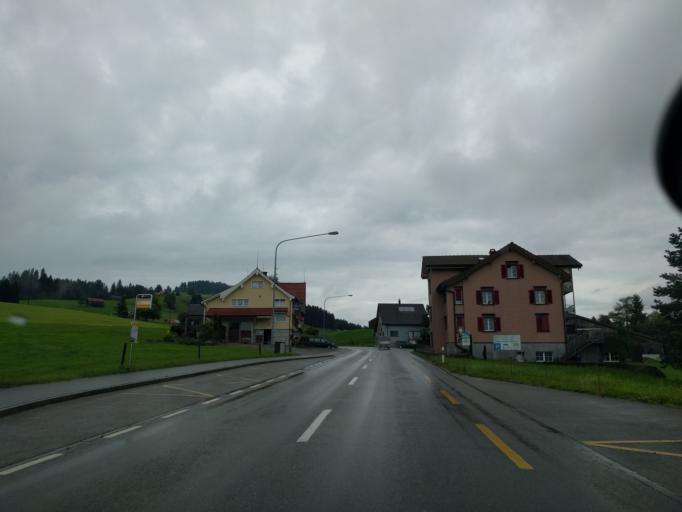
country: CH
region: Appenzell Ausserrhoden
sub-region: Bezirk Hinterland
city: Schwellbrunn
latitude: 47.3339
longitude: 9.2347
